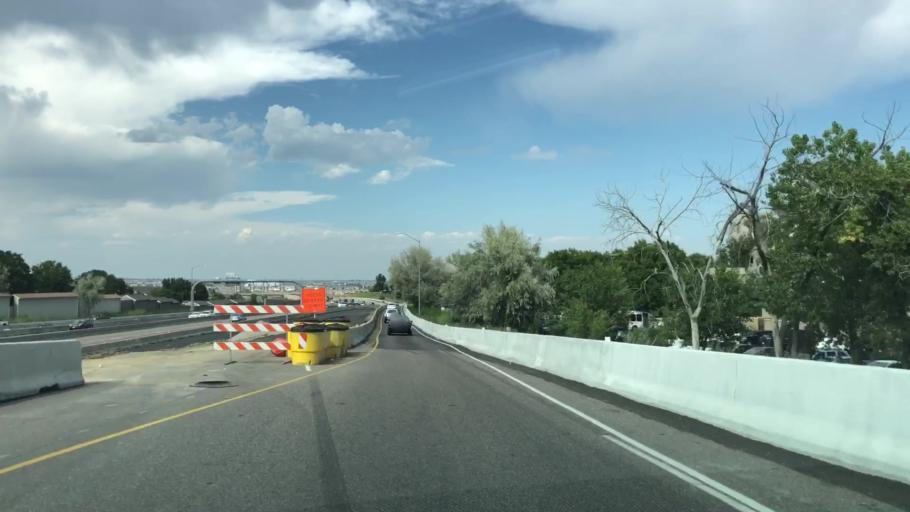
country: US
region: Colorado
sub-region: Adams County
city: Northglenn
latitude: 39.9150
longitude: -104.9887
